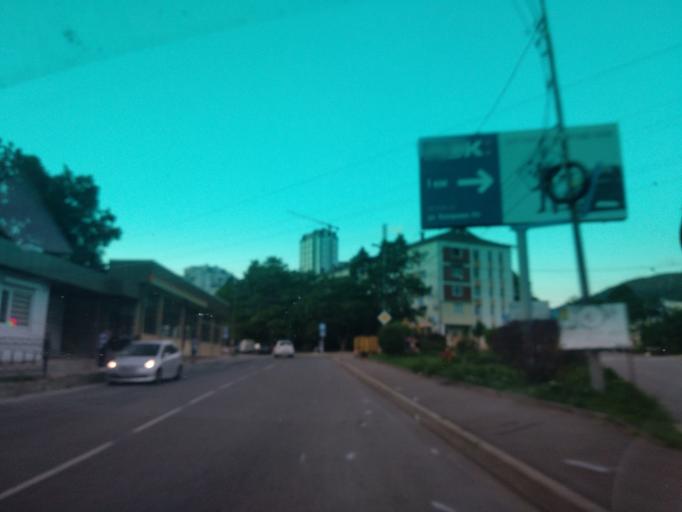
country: RU
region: Krasnodarskiy
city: Tuapse
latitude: 44.1219
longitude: 39.0723
